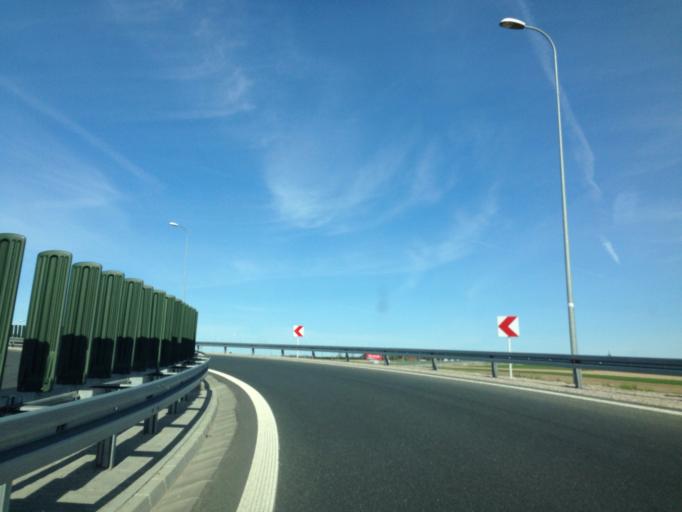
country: PL
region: Lodz Voivodeship
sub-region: Powiat zdunskowolski
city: Zapolice
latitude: 51.5915
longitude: 18.8235
